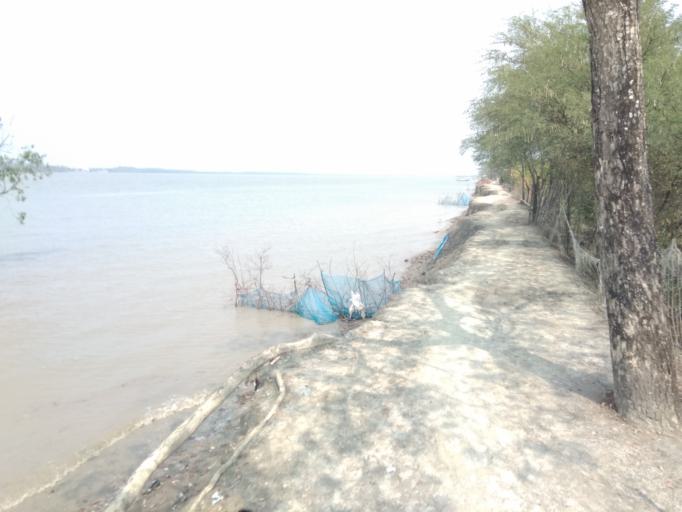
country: IN
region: West Bengal
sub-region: North 24 Parganas
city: Gosaba
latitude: 22.2492
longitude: 89.2500
